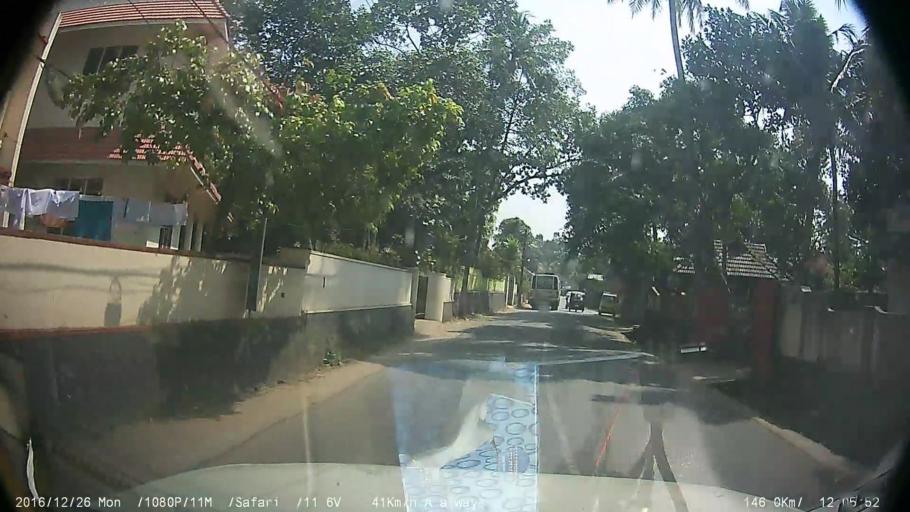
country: IN
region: Kerala
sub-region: Kottayam
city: Changanacheri
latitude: 9.4407
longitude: 76.5581
